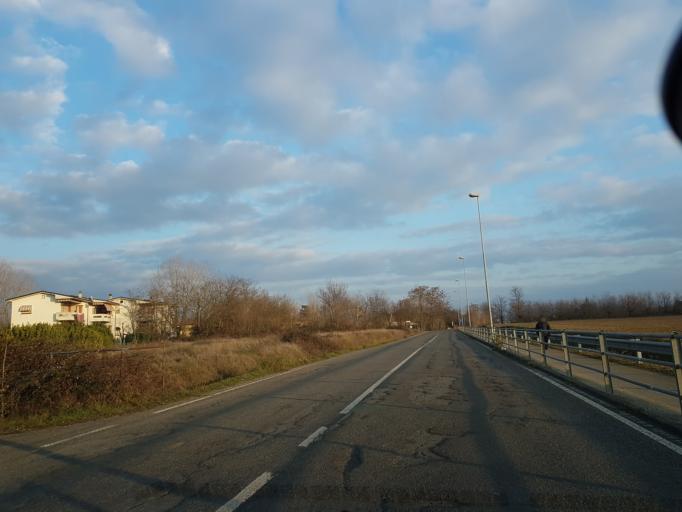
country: IT
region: Piedmont
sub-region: Provincia di Alessandria
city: Pozzolo Formigaro
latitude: 44.7876
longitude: 8.7829
